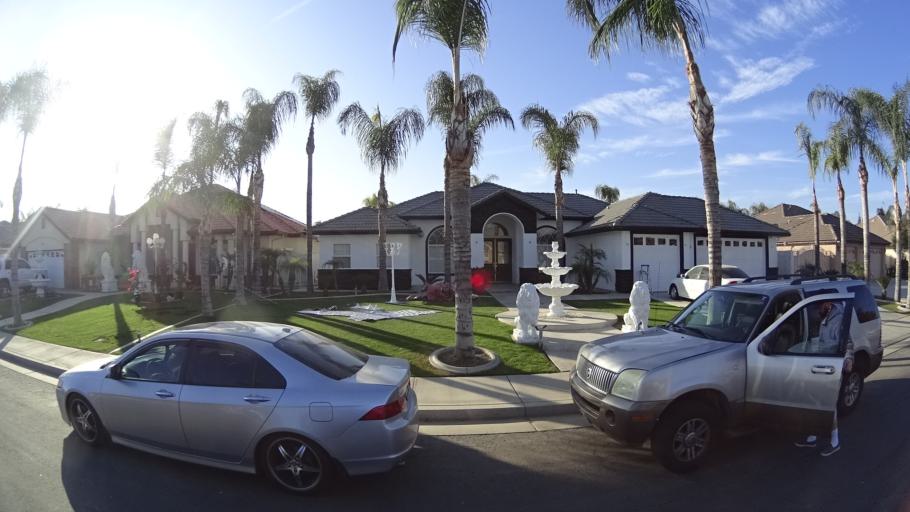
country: US
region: California
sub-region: Kern County
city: Greenfield
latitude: 35.2766
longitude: -119.0555
